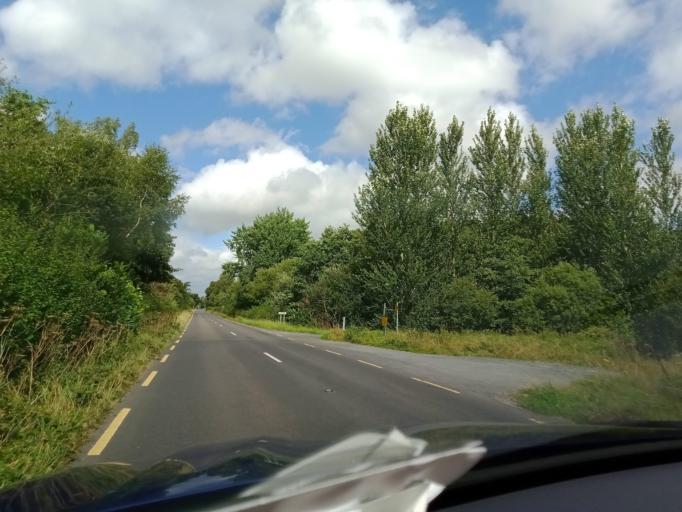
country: IE
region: Leinster
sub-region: Laois
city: Portlaoise
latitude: 52.9847
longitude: -7.2869
